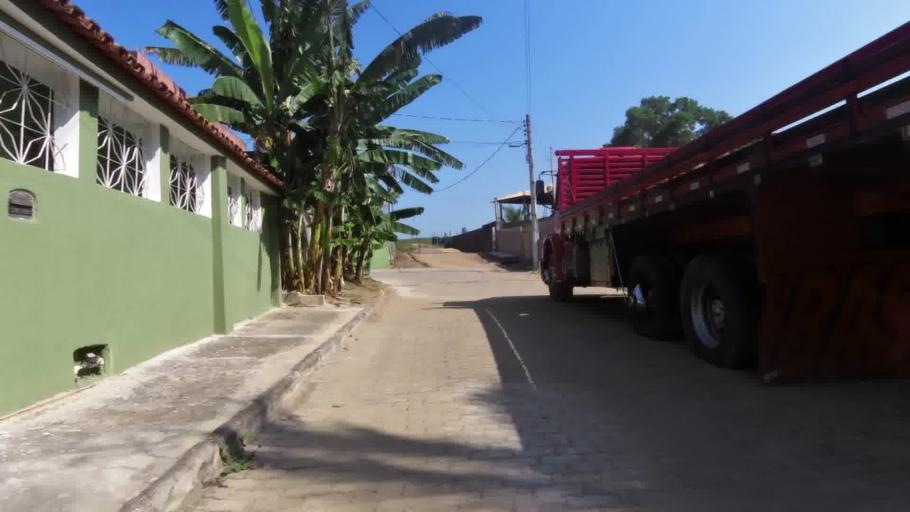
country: BR
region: Espirito Santo
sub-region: Piuma
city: Piuma
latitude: -20.8114
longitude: -40.7390
